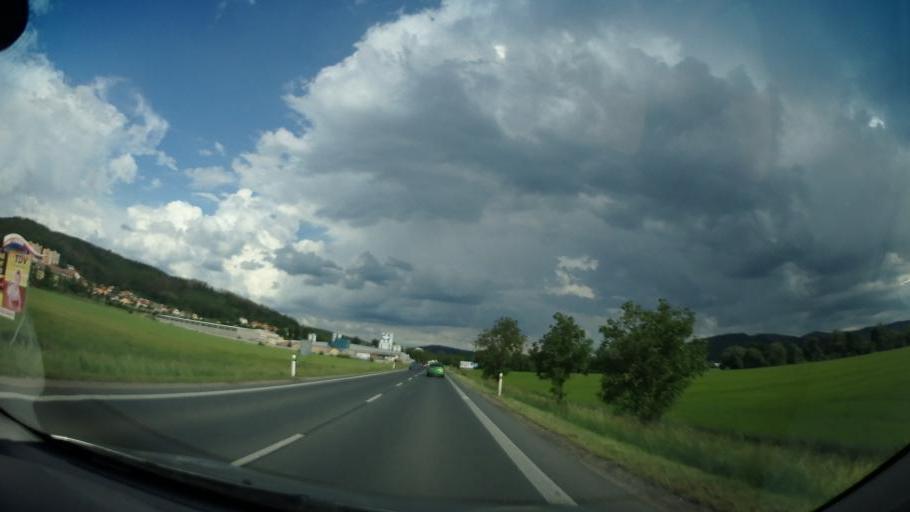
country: CZ
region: South Moravian
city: Tisnov
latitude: 49.3385
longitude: 16.4270
